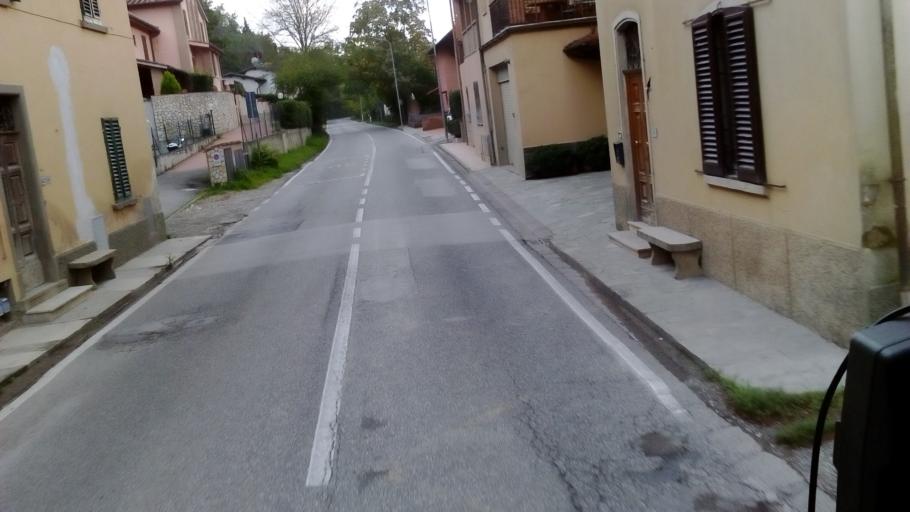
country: IT
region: Tuscany
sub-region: Province of Florence
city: Ginestra Fiorentina
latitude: 43.7018
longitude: 11.0681
